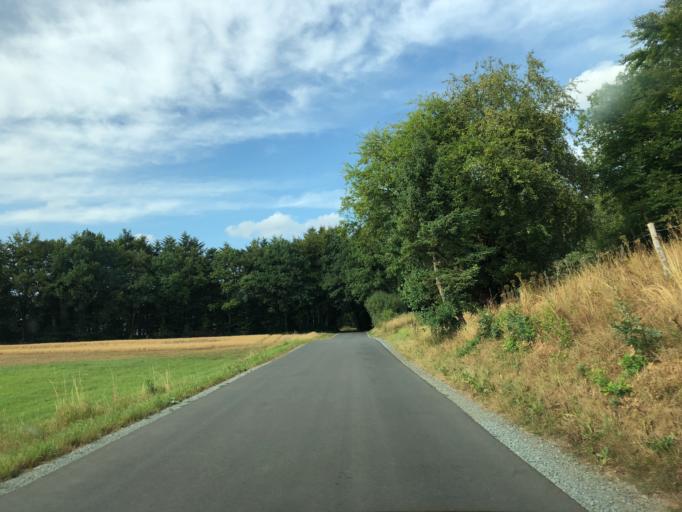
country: DK
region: South Denmark
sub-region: Vejle Kommune
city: Egtved
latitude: 55.6622
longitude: 9.2582
